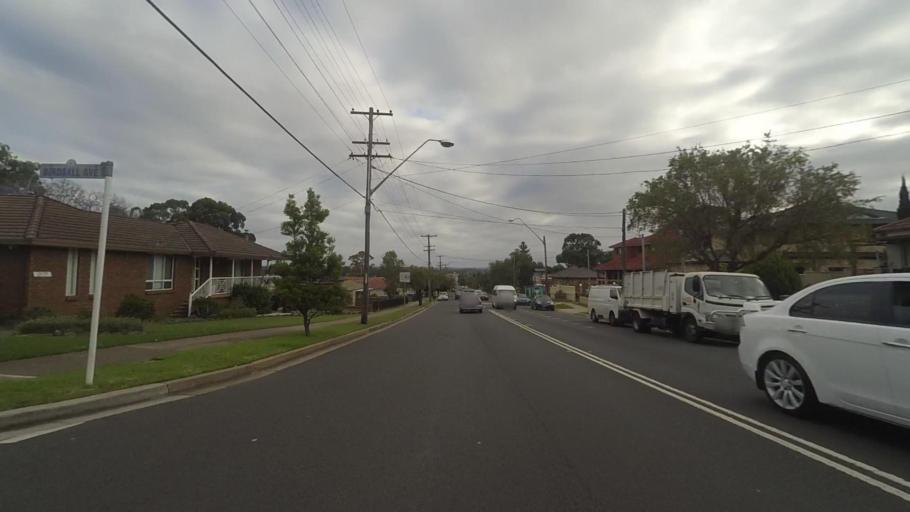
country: AU
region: New South Wales
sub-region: Bankstown
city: Bankstown
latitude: -33.9260
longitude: 151.0125
